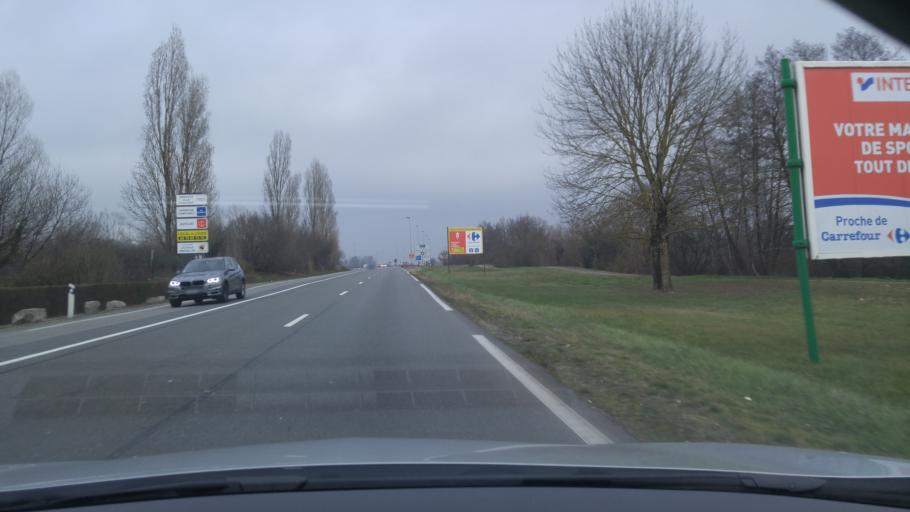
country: FR
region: Rhone-Alpes
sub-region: Departement de l'Isere
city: La Verpilliere
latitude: 45.6281
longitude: 5.1600
